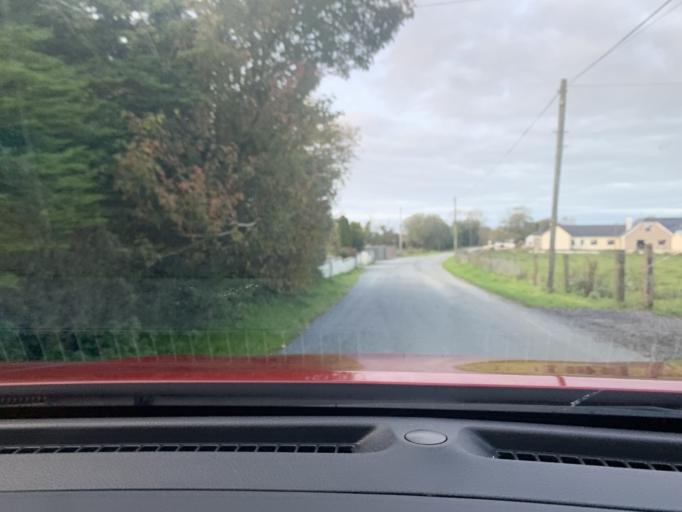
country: IE
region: Connaught
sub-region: Roscommon
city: Ballaghaderreen
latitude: 53.9832
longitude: -8.6156
